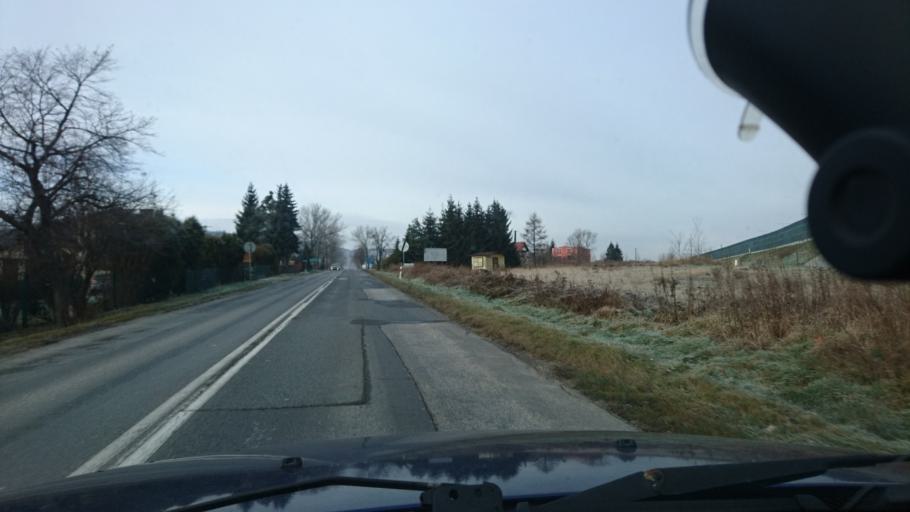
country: PL
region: Silesian Voivodeship
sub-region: Powiat bielski
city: Rybarzowice
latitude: 49.7342
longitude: 19.1140
